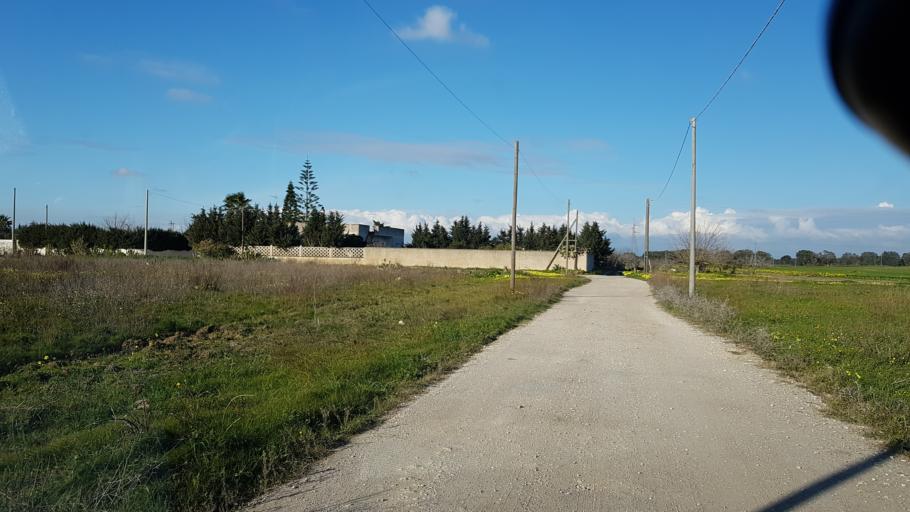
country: IT
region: Apulia
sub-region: Provincia di Brindisi
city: Tuturano
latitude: 40.5433
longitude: 17.9587
